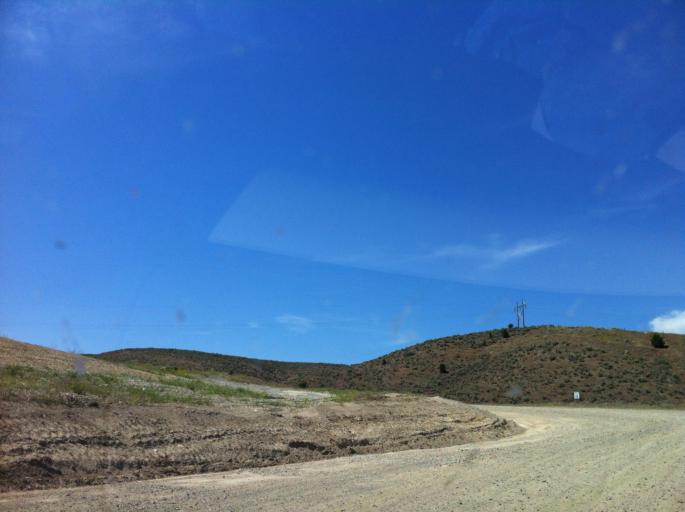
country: US
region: Oregon
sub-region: Baker County
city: Baker City
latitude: 44.7054
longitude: -117.7836
